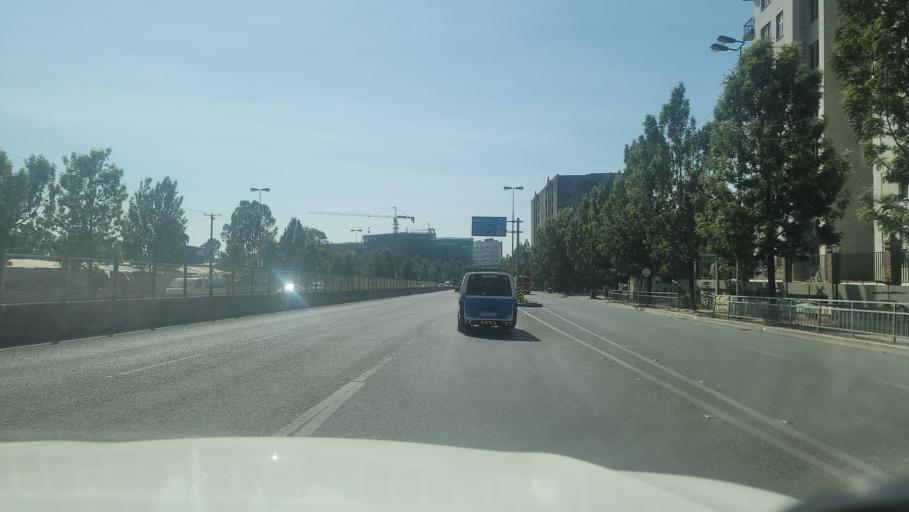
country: ET
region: Adis Abeba
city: Addis Ababa
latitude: 9.0152
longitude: 38.8029
